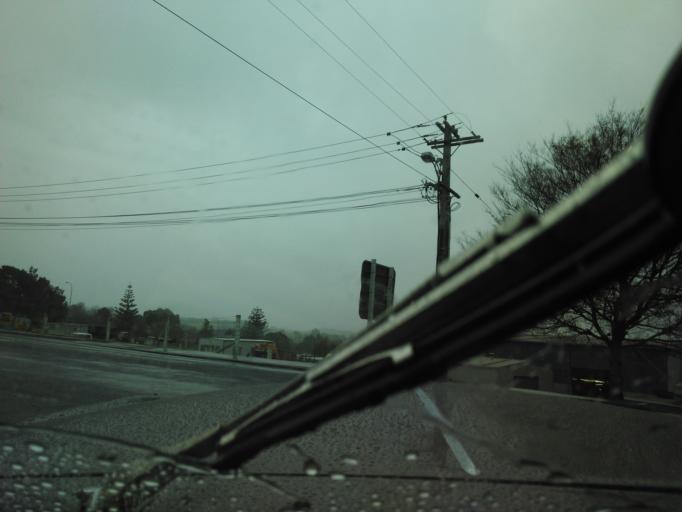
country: NZ
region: Auckland
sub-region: Auckland
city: Wellsford
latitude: -36.2970
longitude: 174.5228
